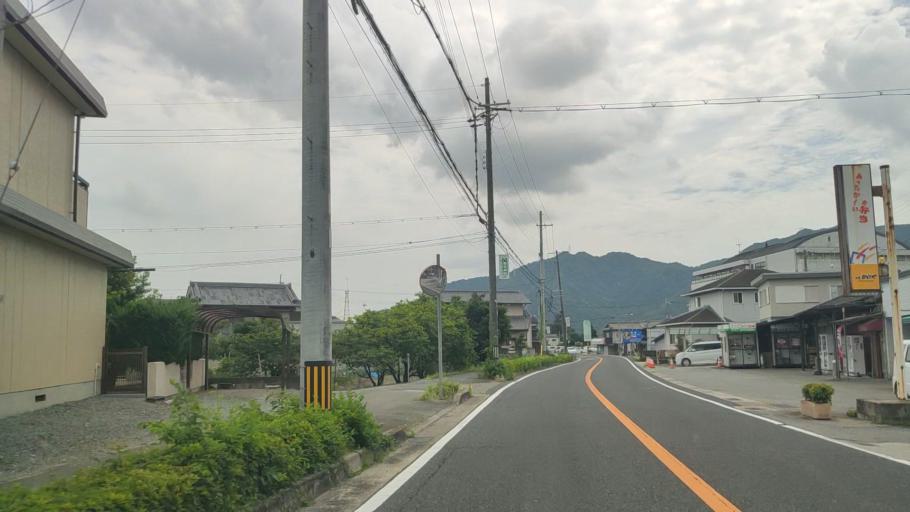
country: JP
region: Hyogo
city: Tatsunocho-tominaga
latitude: 34.9062
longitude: 134.5490
